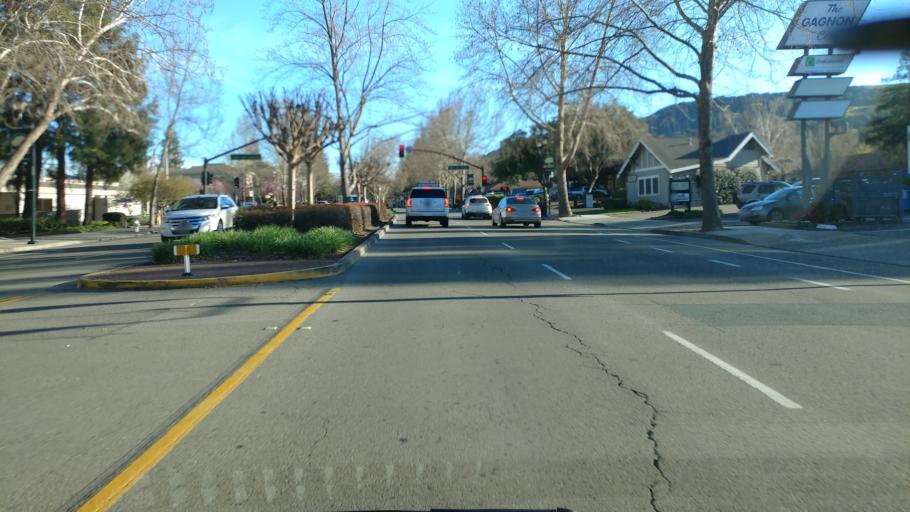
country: US
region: California
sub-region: Contra Costa County
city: Danville
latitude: 37.8162
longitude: -121.9966
